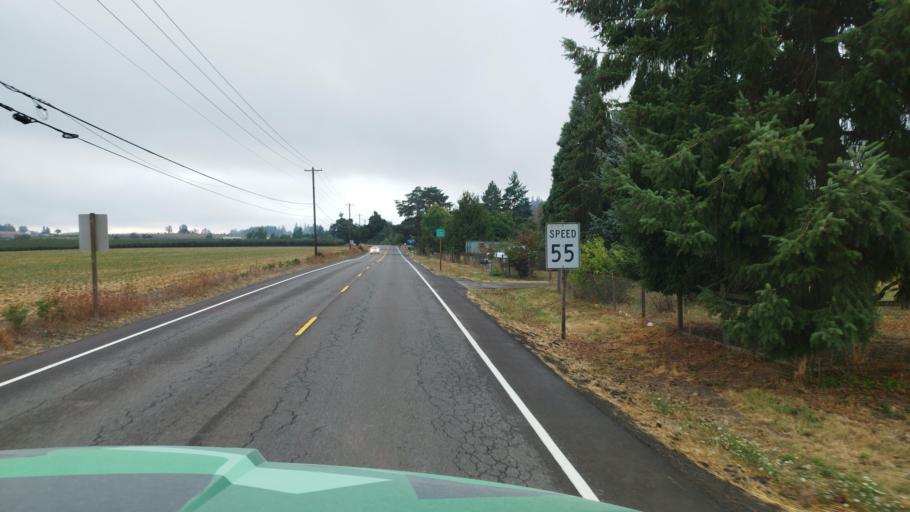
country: US
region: Oregon
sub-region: Yamhill County
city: Yamhill
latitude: 45.3378
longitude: -123.1870
